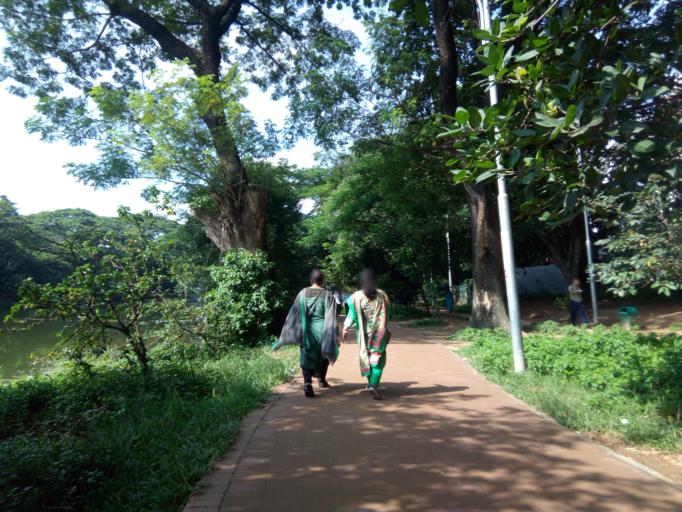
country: BD
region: Dhaka
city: Azimpur
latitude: 23.7478
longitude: 90.3782
